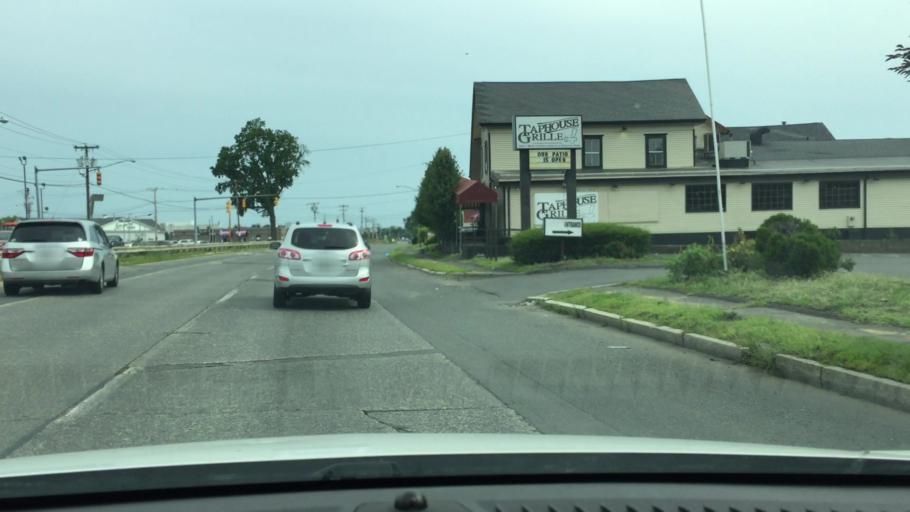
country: US
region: Massachusetts
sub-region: Hampden County
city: Chicopee
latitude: 42.1451
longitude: -72.6291
